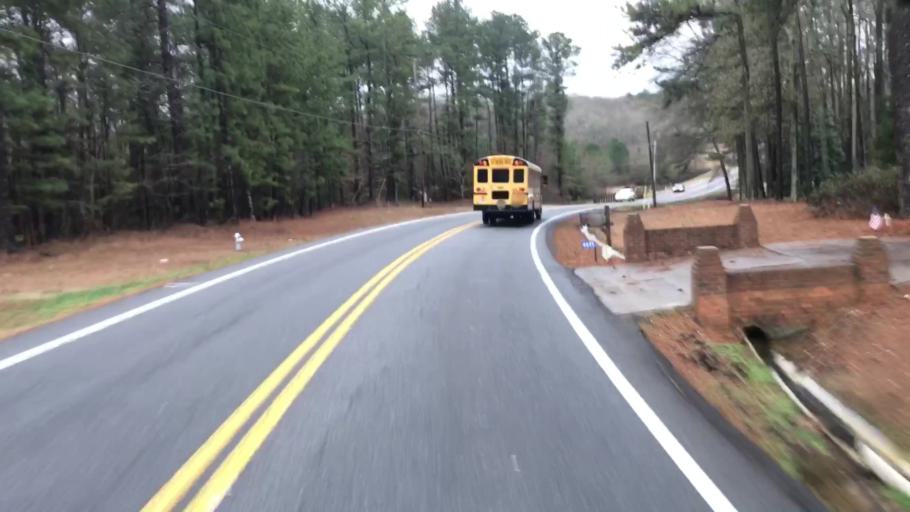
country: US
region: Georgia
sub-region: Gwinnett County
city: Snellville
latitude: 33.8047
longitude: -83.9674
